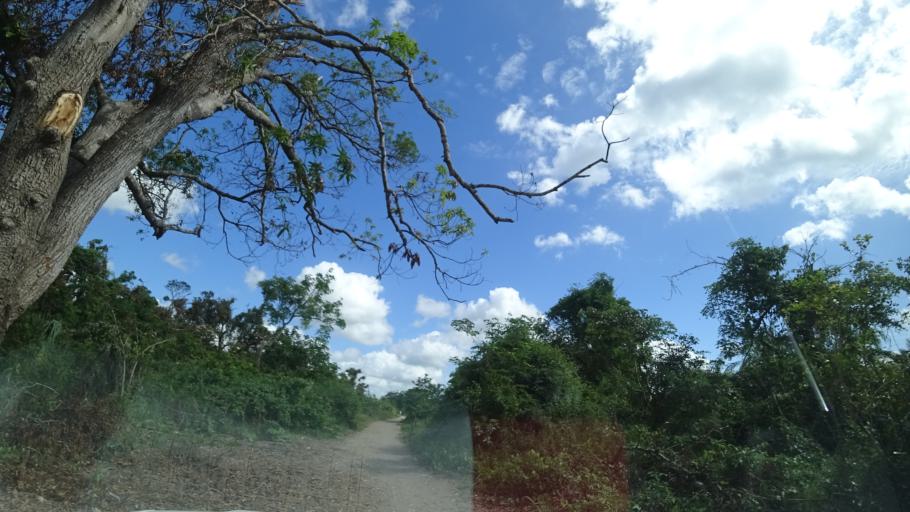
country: MZ
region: Sofala
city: Dondo
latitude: -19.3599
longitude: 34.5733
